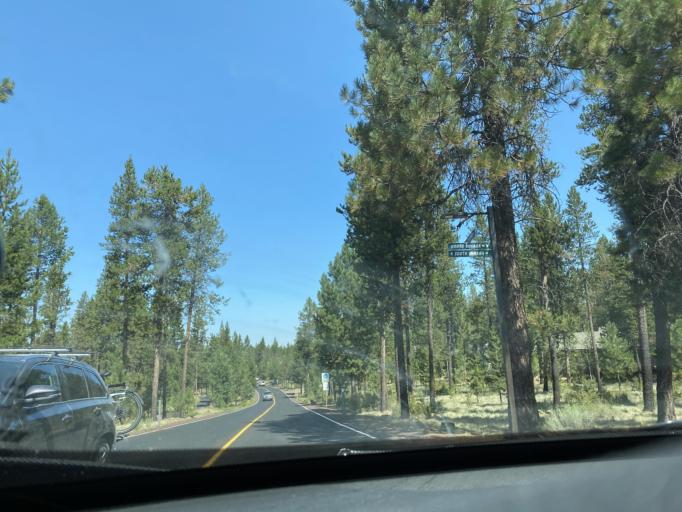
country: US
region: Oregon
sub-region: Deschutes County
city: Sunriver
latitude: 43.8950
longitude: -121.4172
